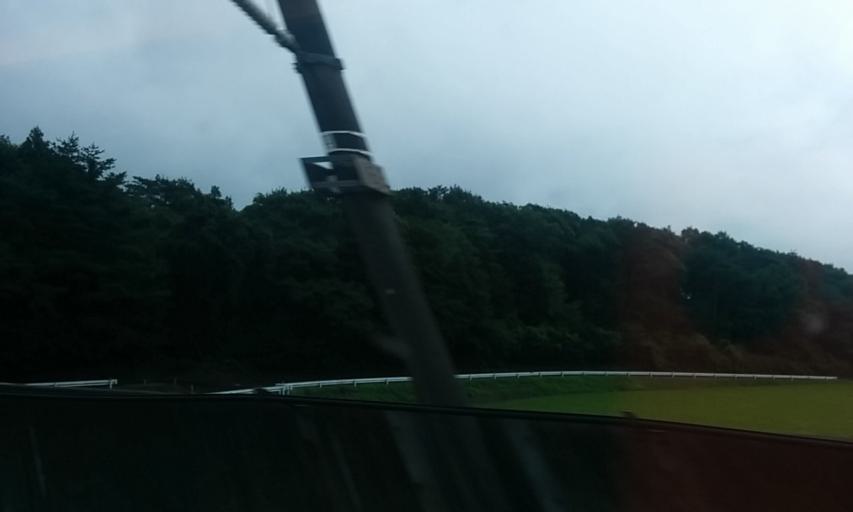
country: JP
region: Tochigi
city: Kuroiso
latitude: 37.0091
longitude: 140.0916
